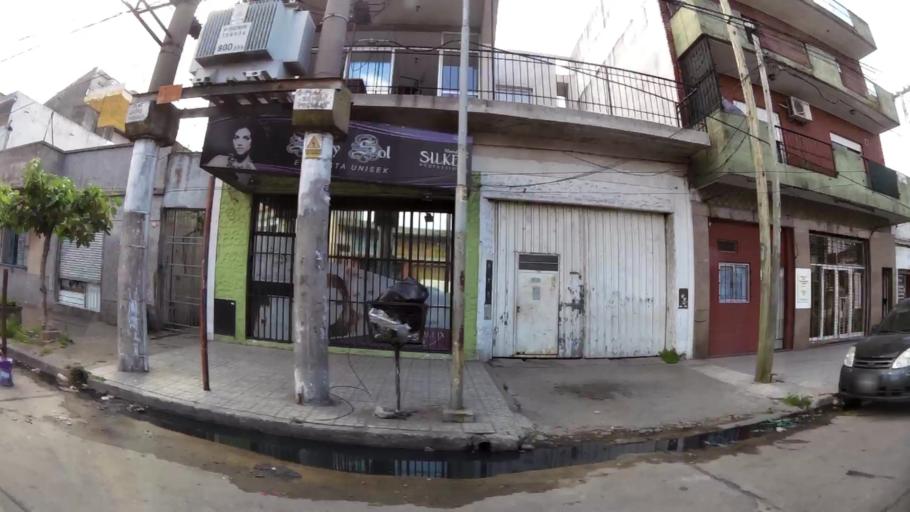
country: AR
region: Buenos Aires
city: San Justo
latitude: -34.6572
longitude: -58.5405
